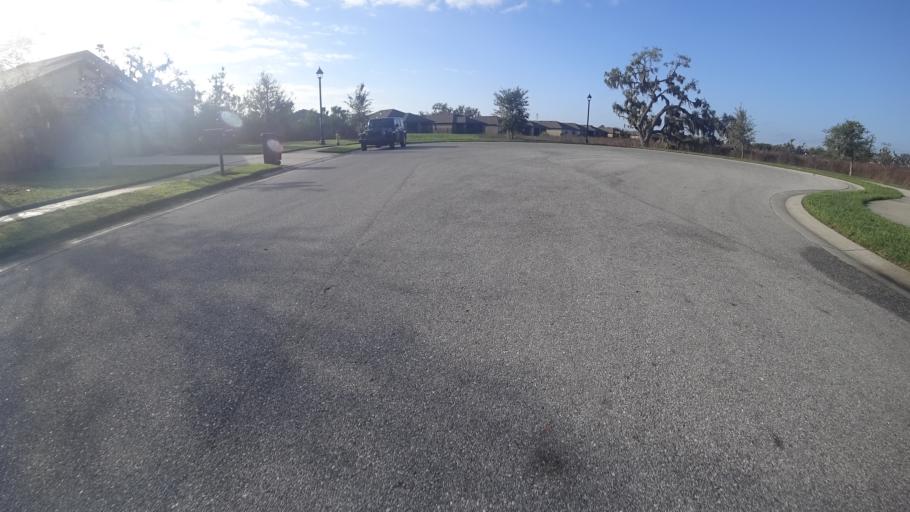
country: US
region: Florida
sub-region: Manatee County
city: Ellenton
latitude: 27.5627
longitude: -82.4558
